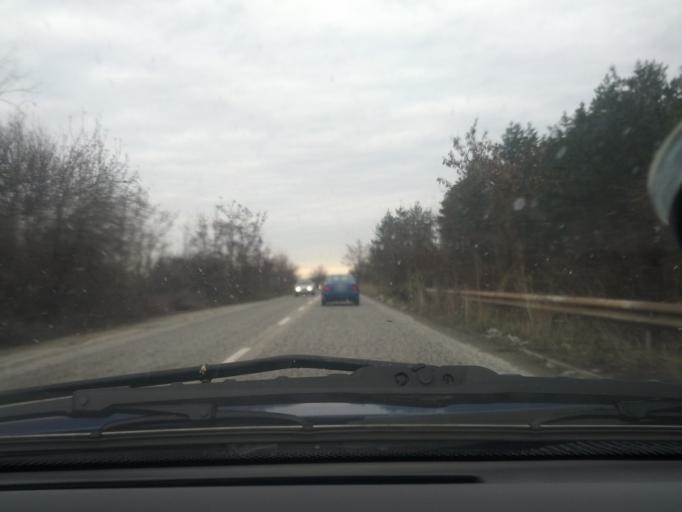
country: BG
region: Vratsa
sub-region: Obshtina Borovan
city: Borovan
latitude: 43.3782
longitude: 23.7124
